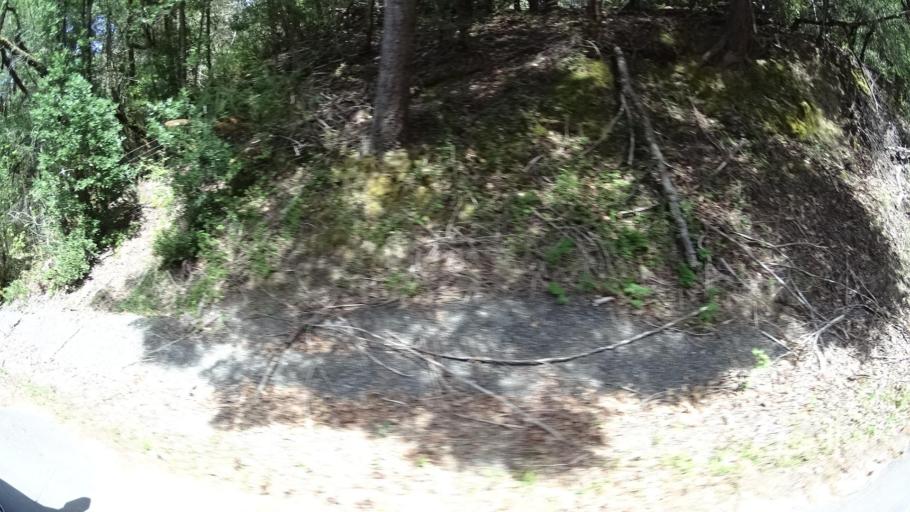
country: US
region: California
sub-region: Humboldt County
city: Redway
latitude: 40.3509
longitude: -123.7172
